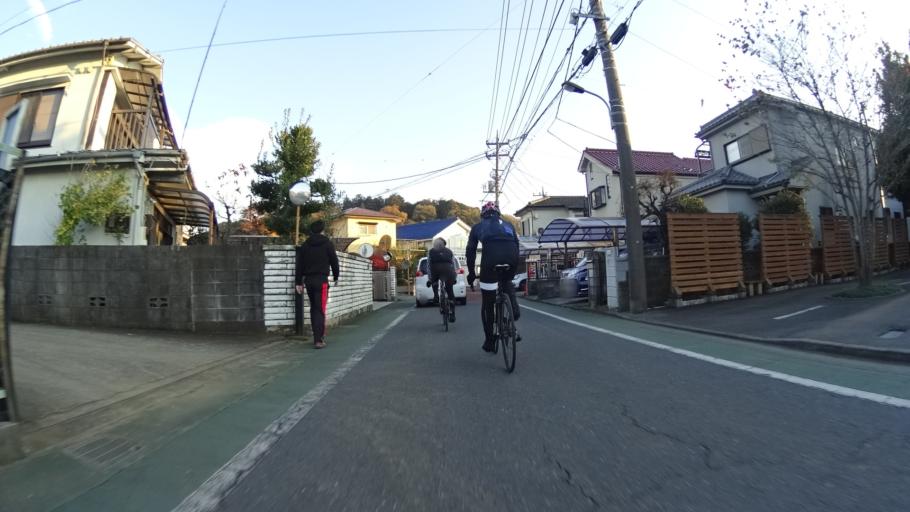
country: JP
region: Tokyo
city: Fussa
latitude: 35.7788
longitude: 139.3492
